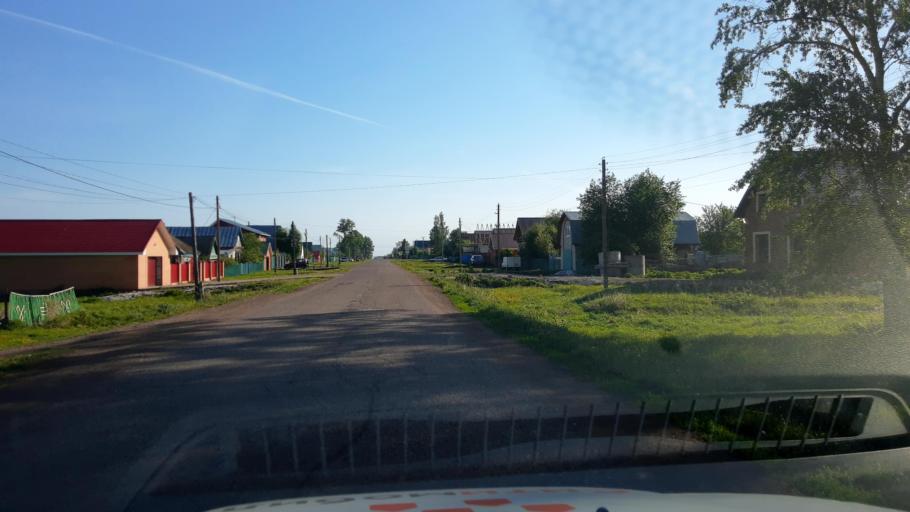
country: RU
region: Bashkortostan
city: Kabakovo
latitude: 54.4553
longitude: 55.9483
